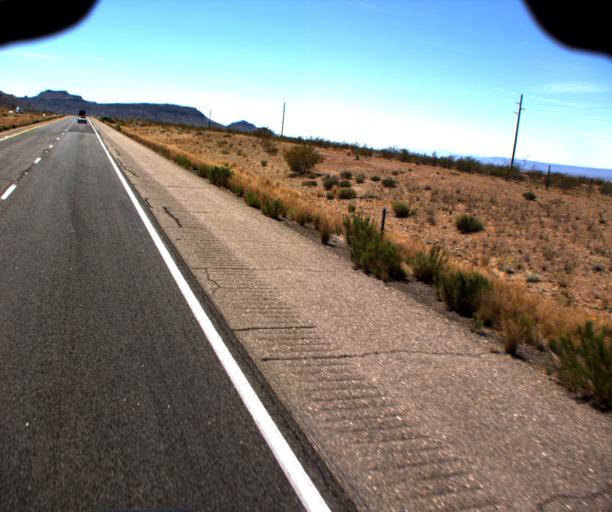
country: US
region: Arizona
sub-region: Mohave County
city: Golden Valley
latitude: 35.2595
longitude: -114.1601
